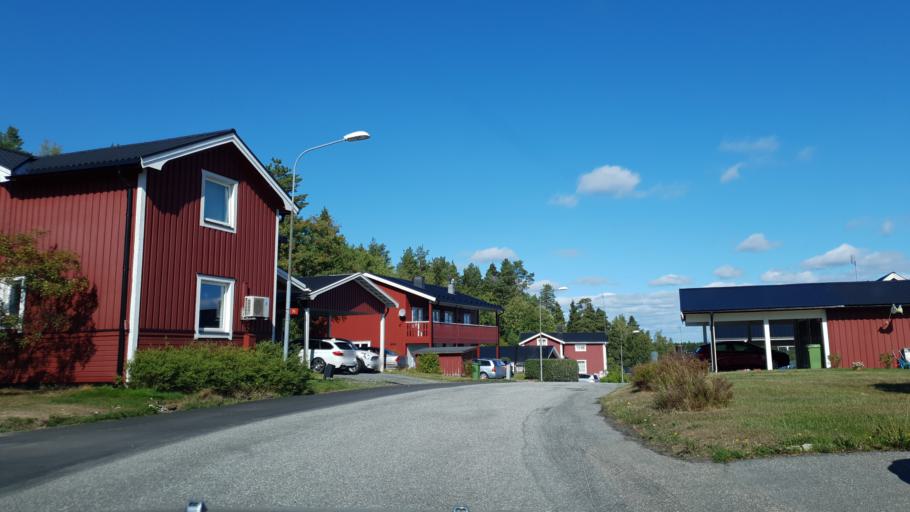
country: SE
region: Vaesterbotten
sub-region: Umea Kommun
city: Holmsund
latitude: 63.7162
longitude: 20.3812
